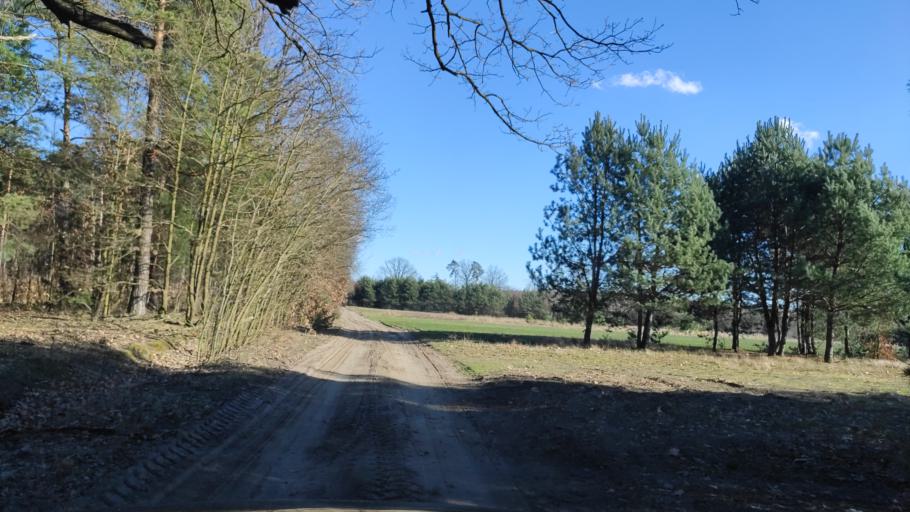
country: PL
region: Masovian Voivodeship
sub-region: Powiat radomski
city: Jedlnia-Letnisko
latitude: 51.4534
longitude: 21.2795
